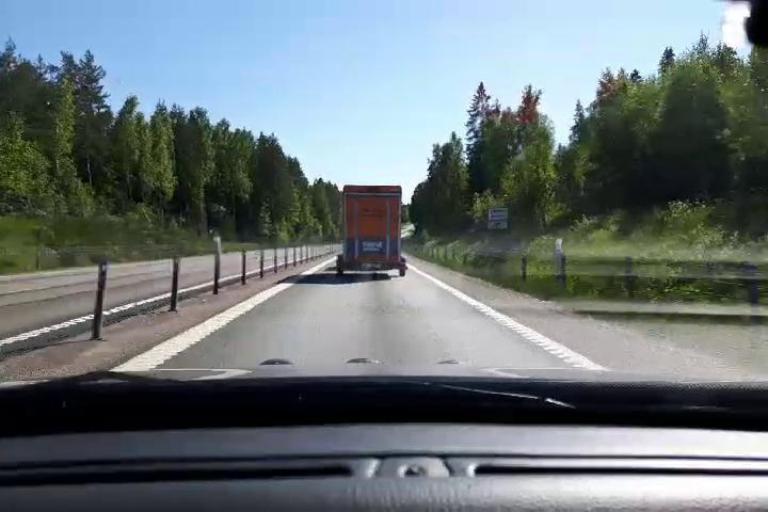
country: SE
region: Gaevleborg
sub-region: Soderhamns Kommun
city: Ljusne
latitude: 61.1420
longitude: 17.0300
